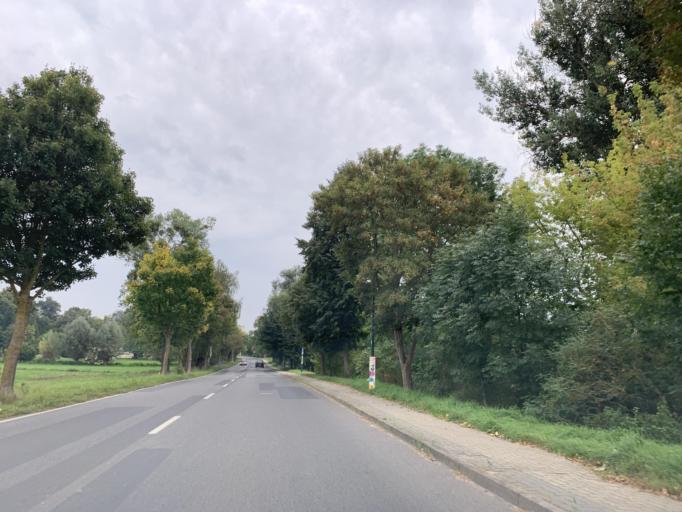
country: DE
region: Brandenburg
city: Mittenwalde
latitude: 53.3324
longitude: 13.7024
